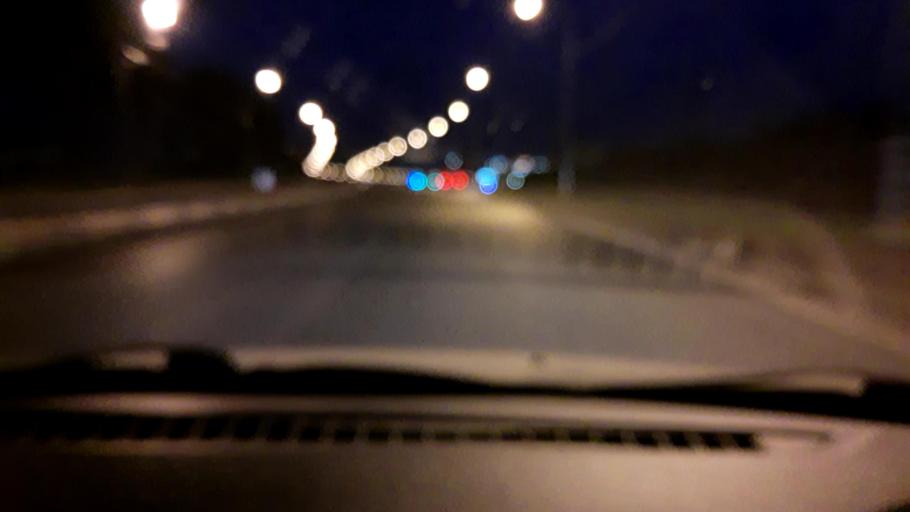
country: RU
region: Nizjnij Novgorod
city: Burevestnik
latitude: 56.1942
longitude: 43.9241
